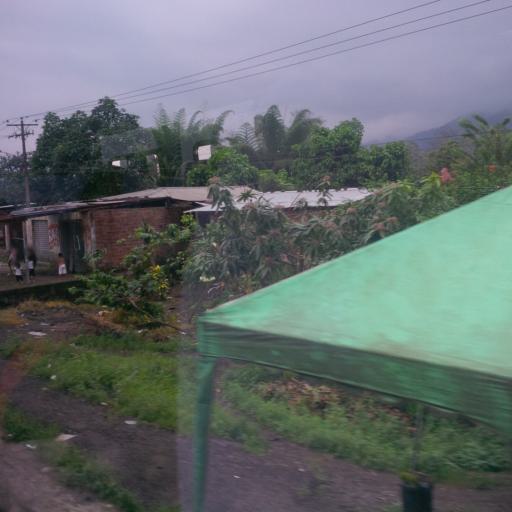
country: EC
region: Canar
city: La Troncal
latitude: -2.2528
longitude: -79.2070
